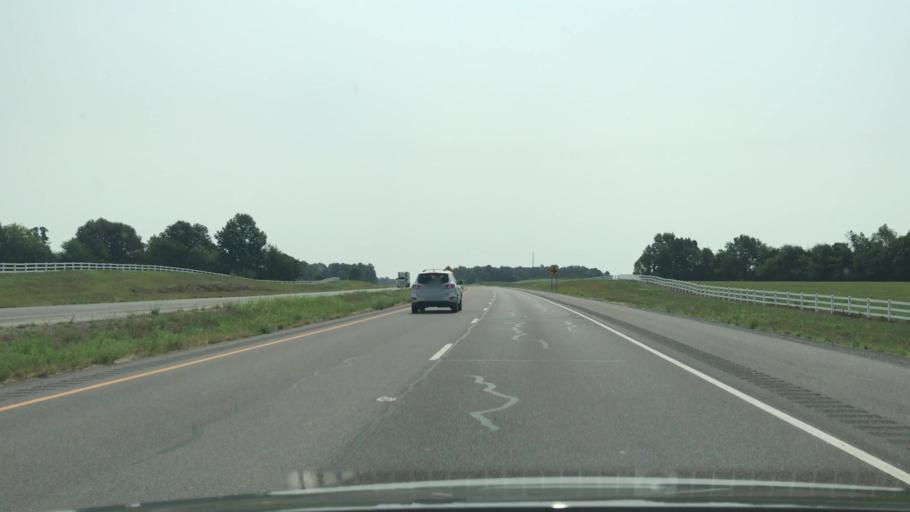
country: US
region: Kentucky
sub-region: Graves County
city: Mayfield
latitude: 36.6794
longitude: -88.5287
